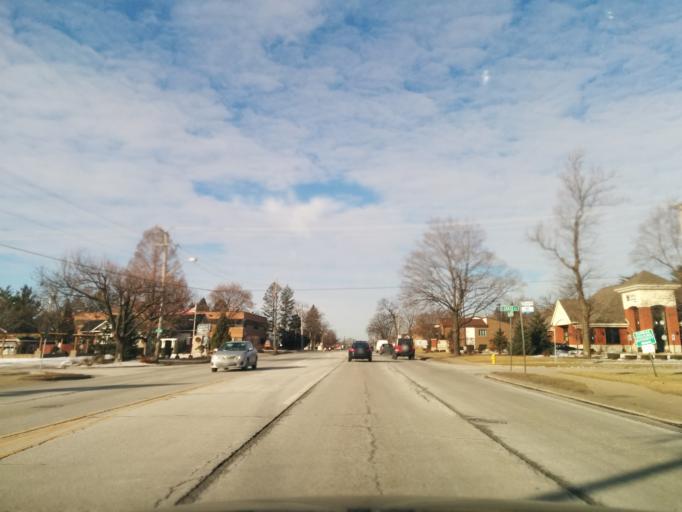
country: US
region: Illinois
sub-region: DuPage County
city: Wheaton
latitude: 41.8590
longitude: -88.0958
